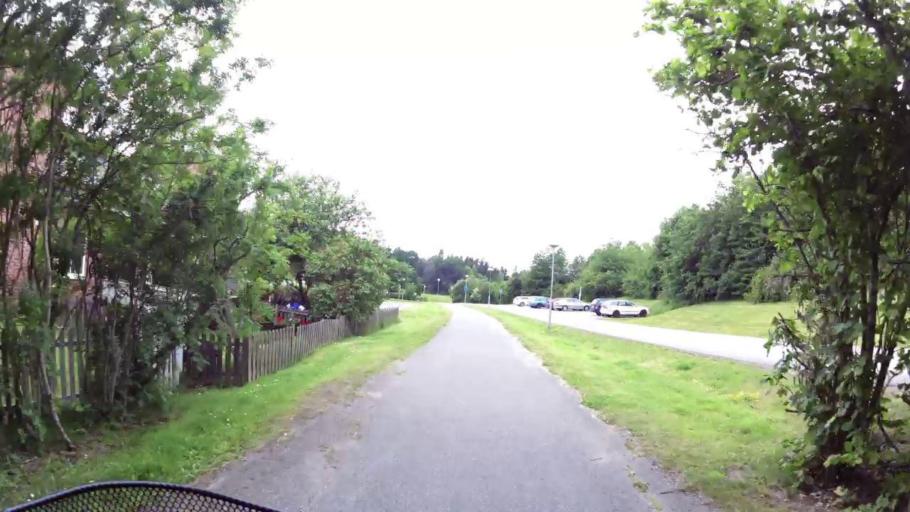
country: SE
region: OEstergoetland
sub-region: Linkopings Kommun
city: Sturefors
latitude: 58.3721
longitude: 15.6807
